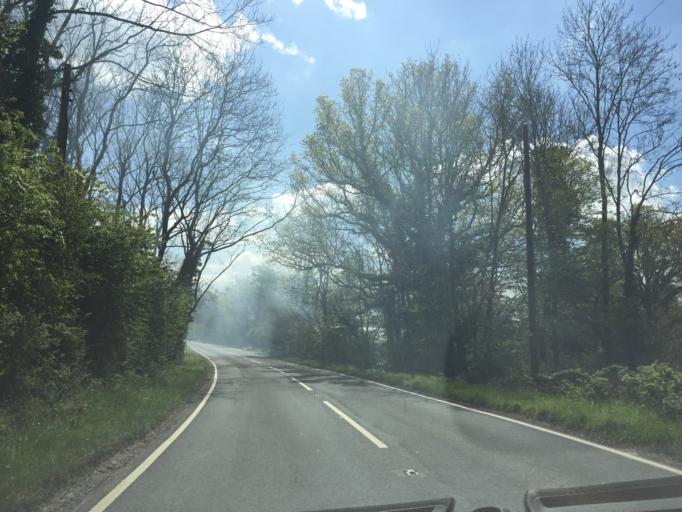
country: GB
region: England
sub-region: Kent
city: Edenbridge
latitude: 51.1309
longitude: 0.1095
